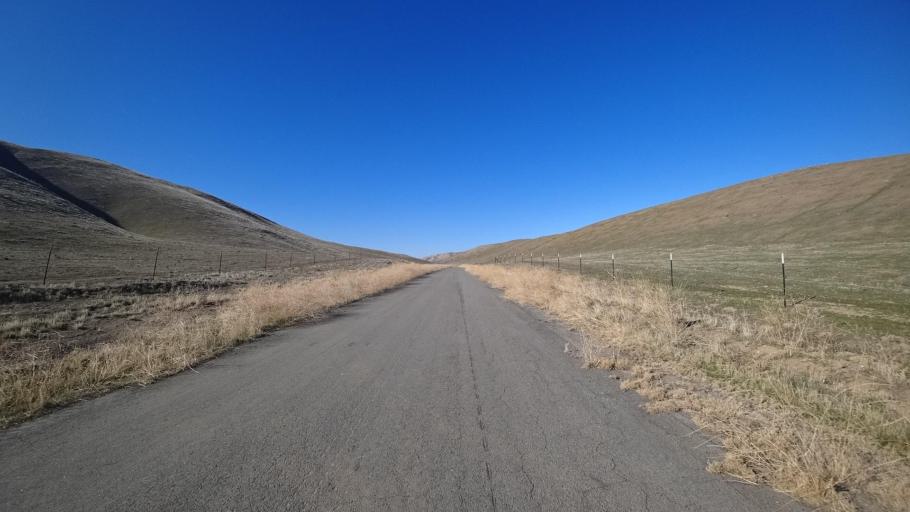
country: US
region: California
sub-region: Kern County
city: Maricopa
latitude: 34.9792
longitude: -119.4658
